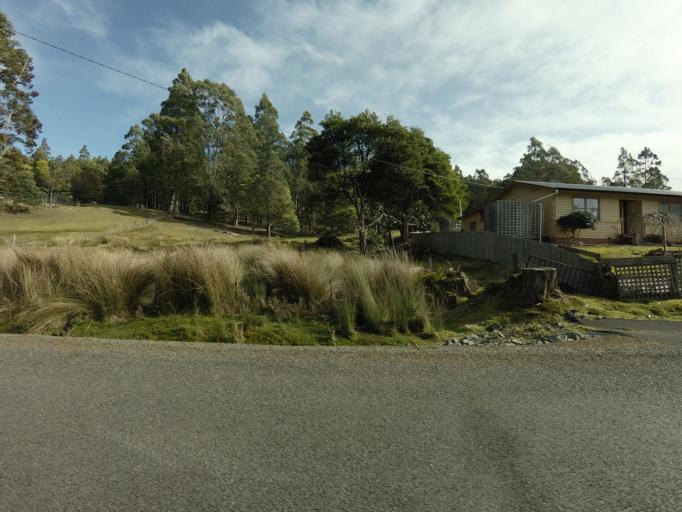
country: AU
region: Tasmania
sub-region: Kingborough
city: Margate
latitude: -43.0133
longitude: 147.1599
